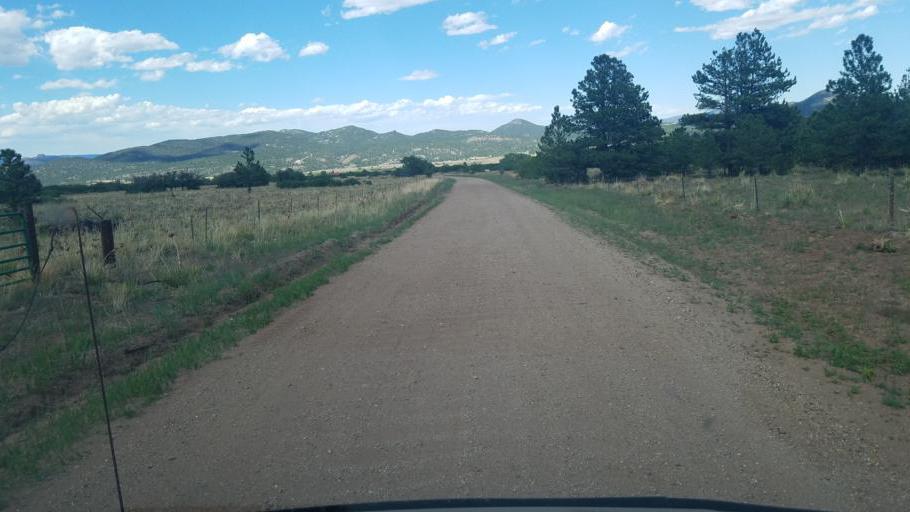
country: US
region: Colorado
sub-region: Custer County
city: Westcliffe
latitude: 38.2221
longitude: -105.6029
